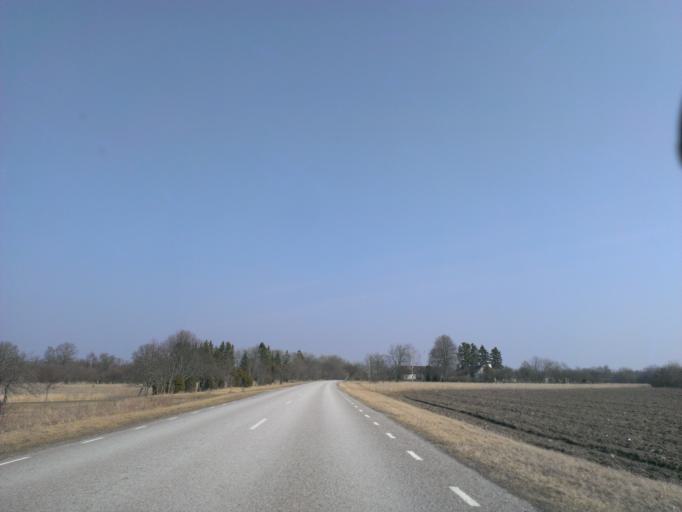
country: EE
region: Saare
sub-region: Kuressaare linn
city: Kuressaare
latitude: 58.2832
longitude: 22.6485
